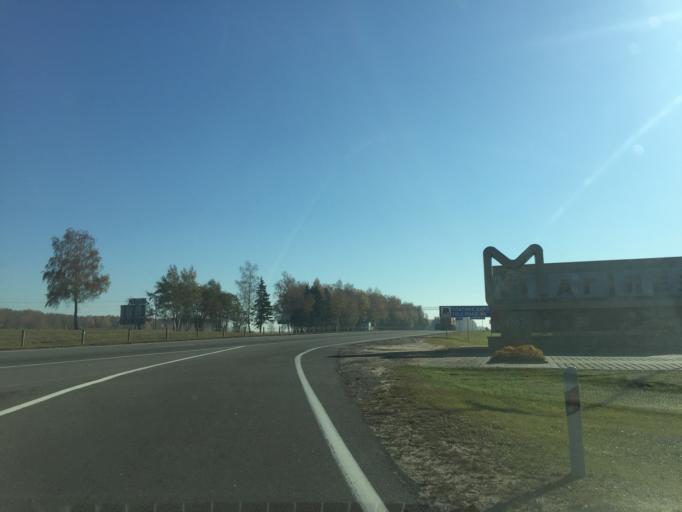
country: BY
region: Mogilev
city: Buynichy
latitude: 53.9472
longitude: 30.2259
